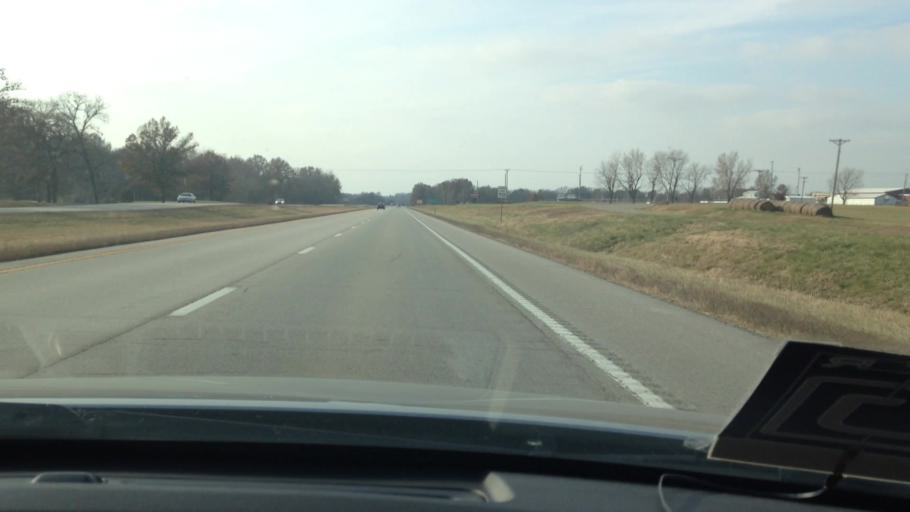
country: US
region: Missouri
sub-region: Cass County
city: Garden City
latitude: 38.5041
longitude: -94.0823
